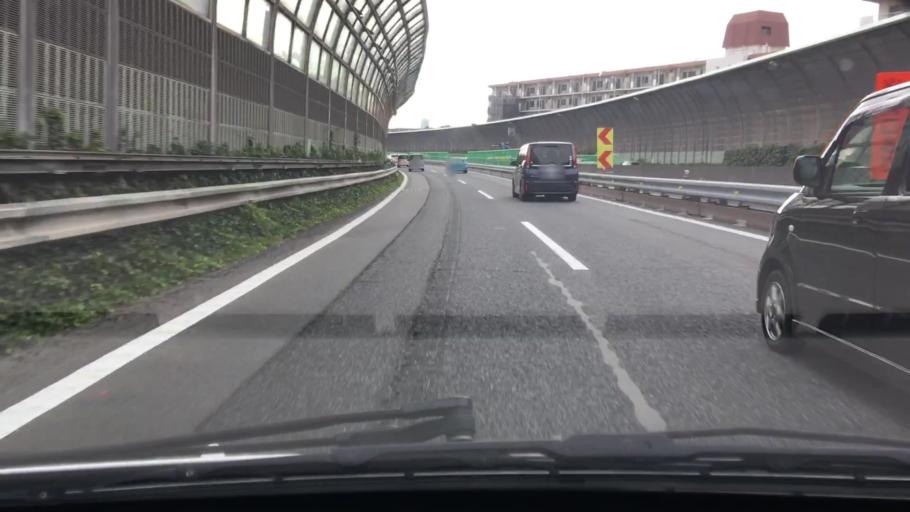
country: JP
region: Chiba
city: Funabashi
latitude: 35.6772
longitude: 140.0131
